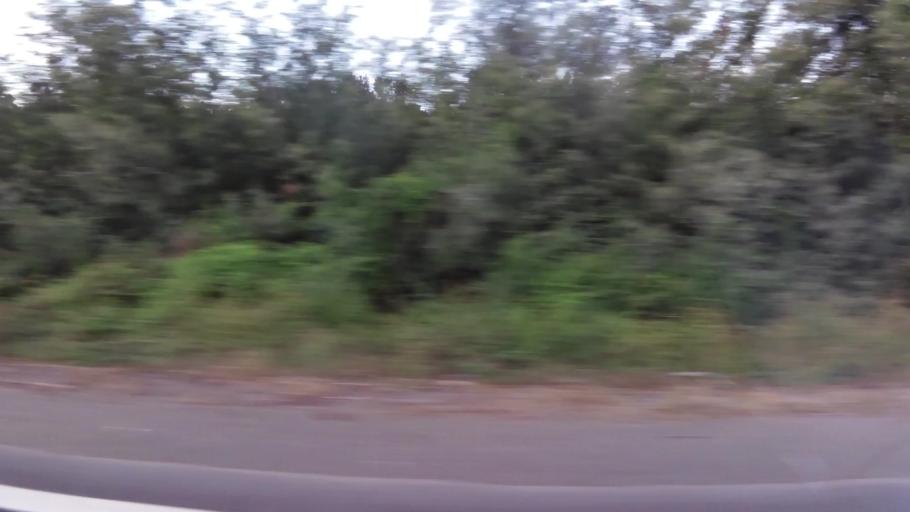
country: CL
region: Biobio
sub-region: Provincia de Concepcion
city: Concepcion
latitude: -36.8637
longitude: -73.0459
